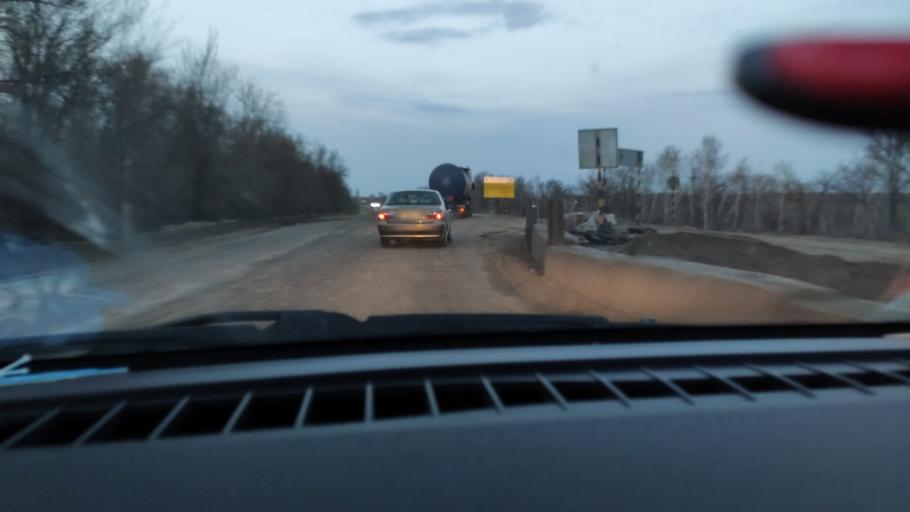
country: RU
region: Saratov
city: Sinodskoye
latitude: 52.0249
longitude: 46.7131
